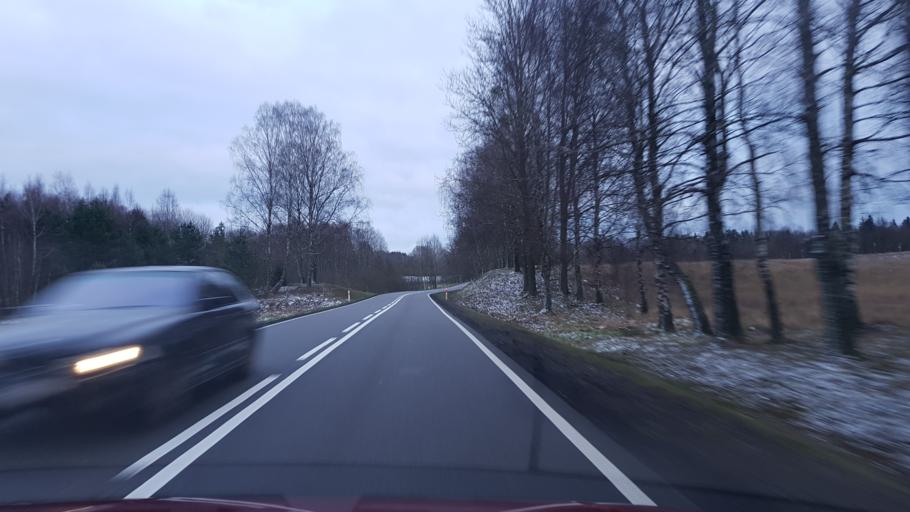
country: PL
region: Pomeranian Voivodeship
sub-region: Powiat bytowski
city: Tuchomie
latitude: 54.0499
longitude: 17.2182
